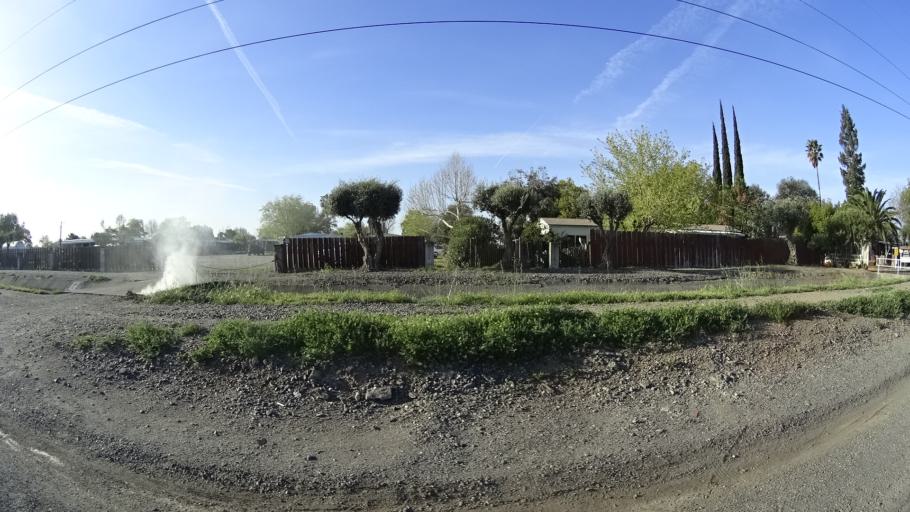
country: US
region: California
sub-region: Glenn County
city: Orland
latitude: 39.7405
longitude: -122.2103
